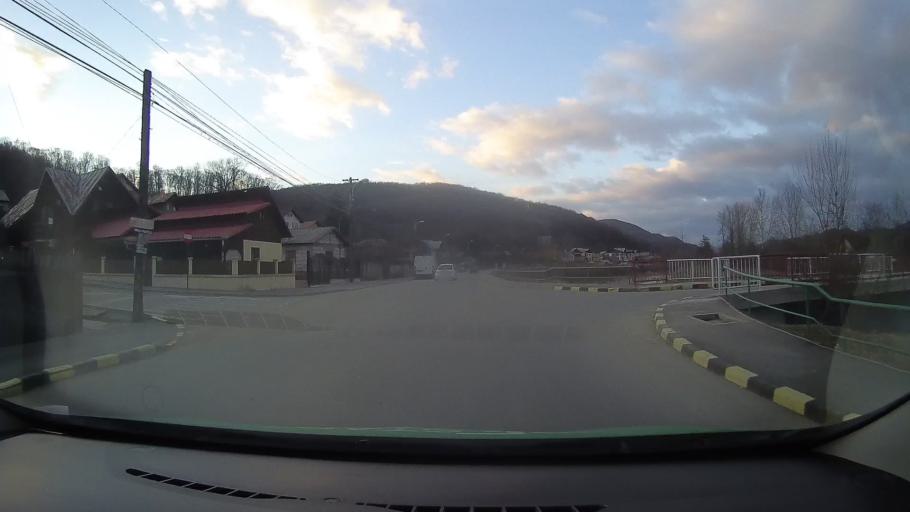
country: RO
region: Dambovita
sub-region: Municipiul Moreni
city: Moreni
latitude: 44.9912
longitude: 25.6365
